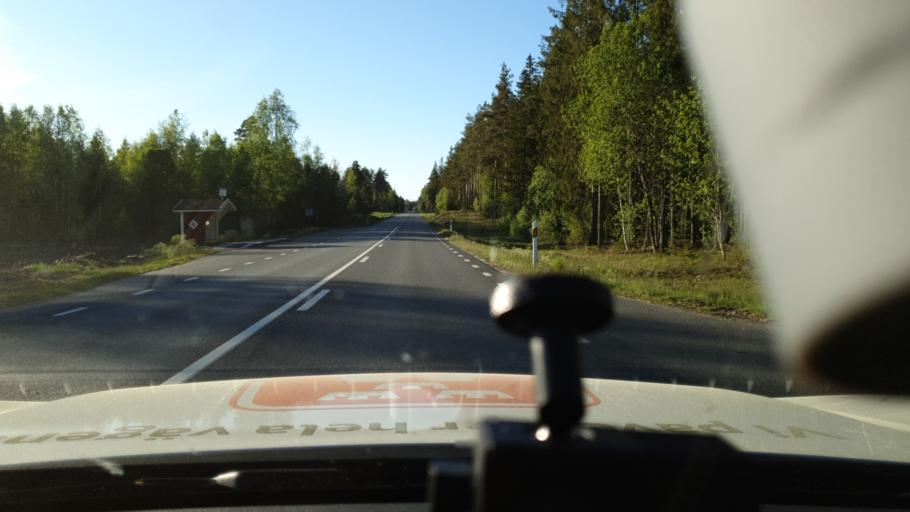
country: SE
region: Joenkoeping
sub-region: Vetlanda Kommun
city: Ekenassjon
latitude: 57.5571
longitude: 14.9812
